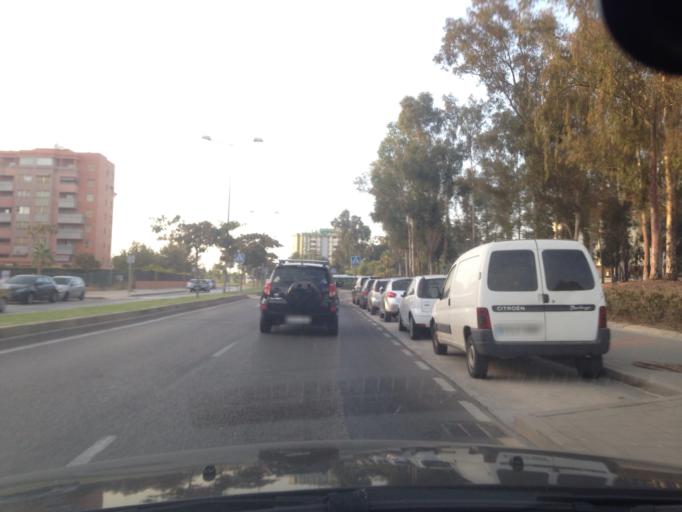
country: ES
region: Andalusia
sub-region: Provincia de Malaga
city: Malaga
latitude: 36.7187
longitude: -4.4839
